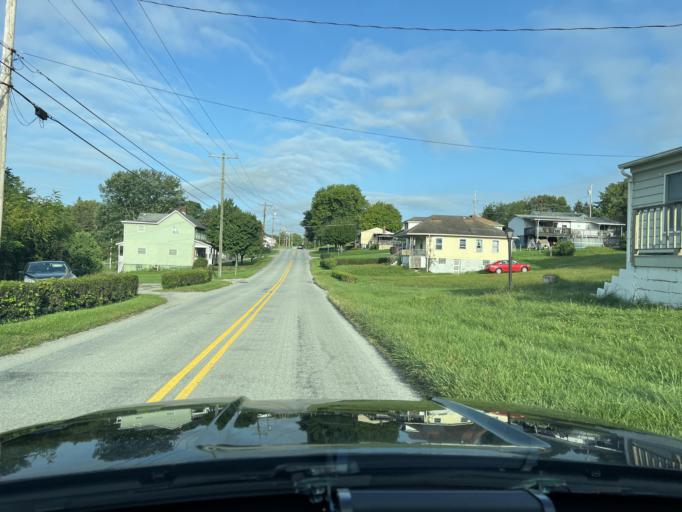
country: US
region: Pennsylvania
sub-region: Fayette County
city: Leith-Hatfield
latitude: 39.8798
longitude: -79.7311
